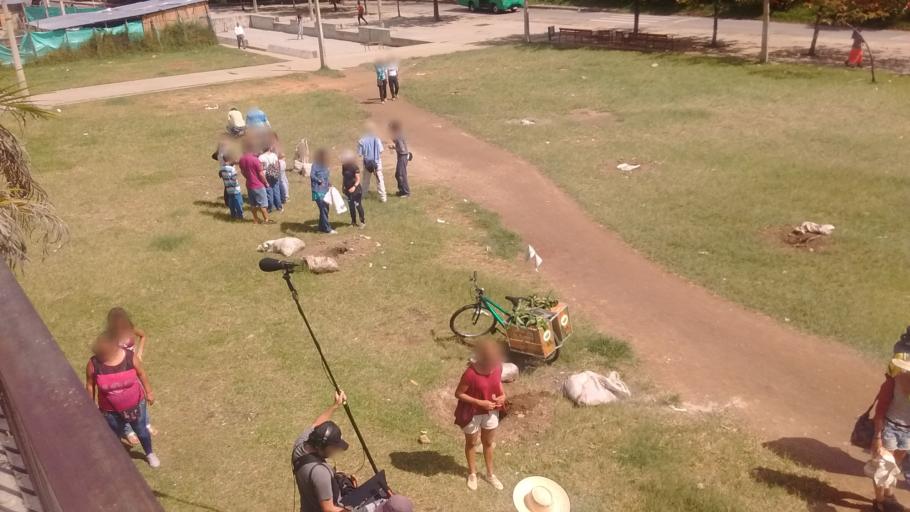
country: CO
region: Antioquia
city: Medellin
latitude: 6.2530
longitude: -75.6231
